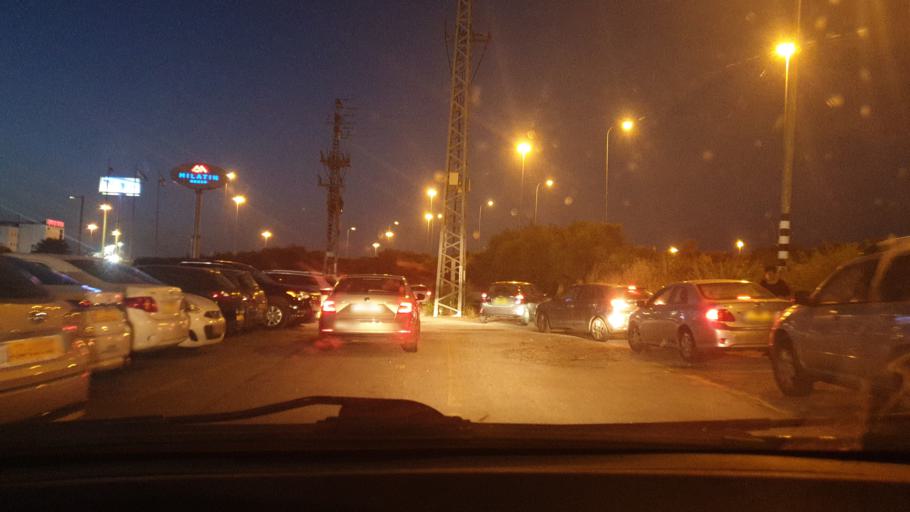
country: IL
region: Central District
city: Bene 'Ayish
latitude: 31.8003
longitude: 34.7623
